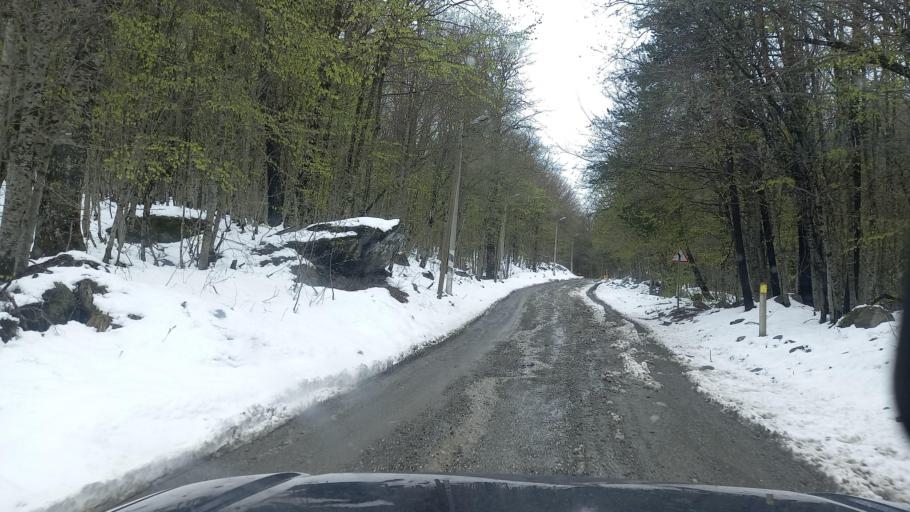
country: RU
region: North Ossetia
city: Mizur
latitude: 42.7892
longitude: 43.9045
